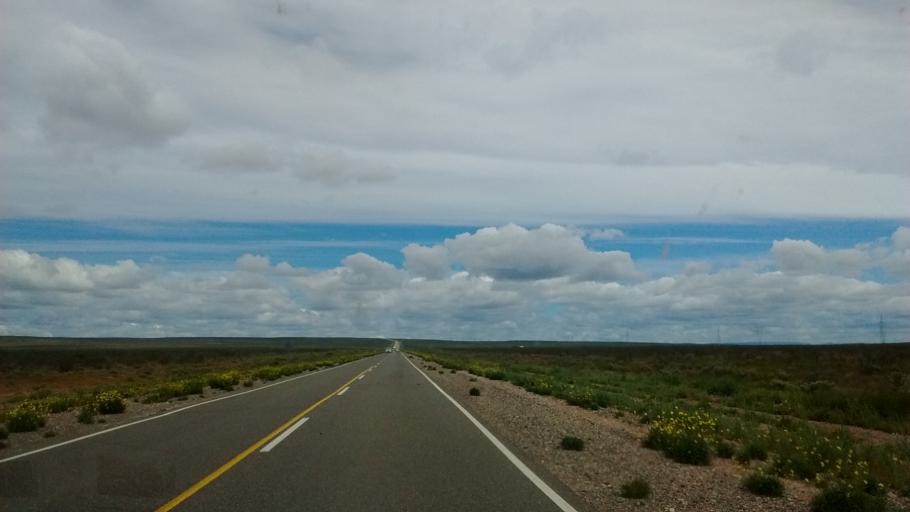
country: AR
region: Neuquen
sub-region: Departamento de Picun Leufu
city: Picun Leufu
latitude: -39.7132
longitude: -69.5187
